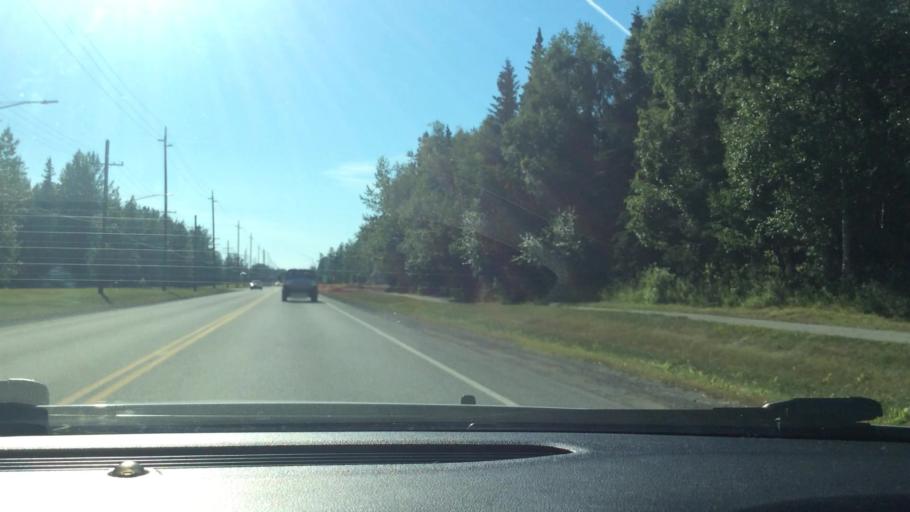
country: US
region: Alaska
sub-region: Anchorage Municipality
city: Elmendorf Air Force Base
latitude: 61.2314
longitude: -149.7518
